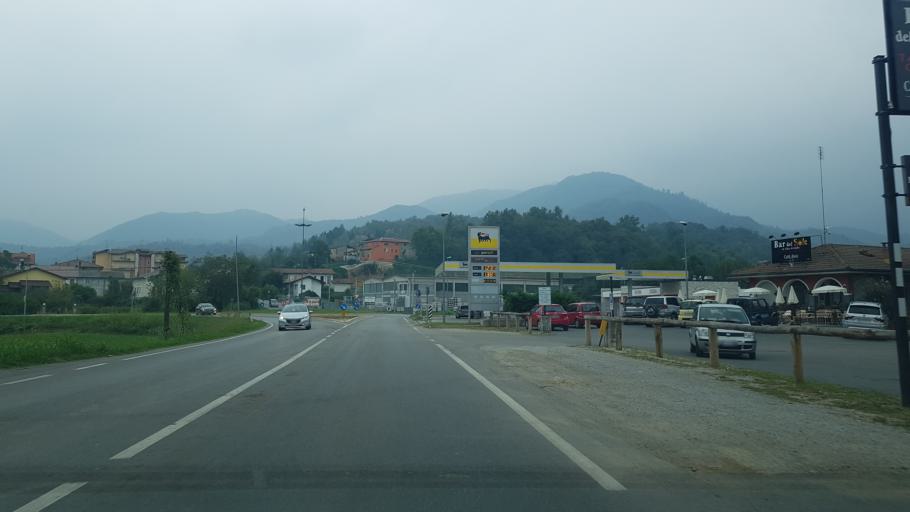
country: IT
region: Piedmont
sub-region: Provincia di Cuneo
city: Villanova Mondovi
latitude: 44.3410
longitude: 7.7777
